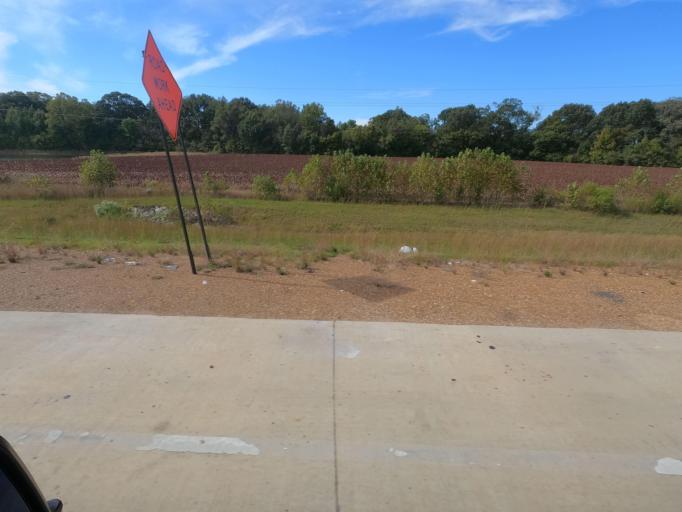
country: US
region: Tennessee
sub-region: Shelby County
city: Arlington
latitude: 35.2916
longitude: -89.6133
